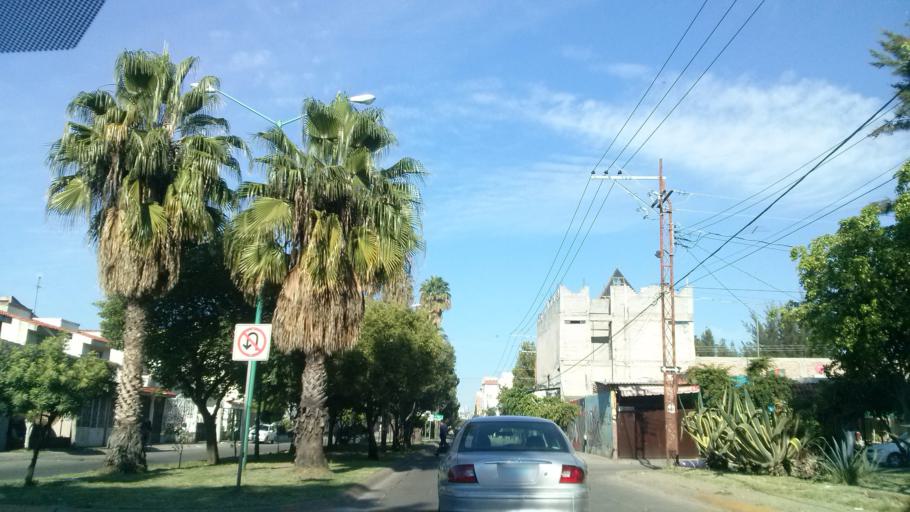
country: MX
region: Guanajuato
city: Leon
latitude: 21.1338
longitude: -101.6540
